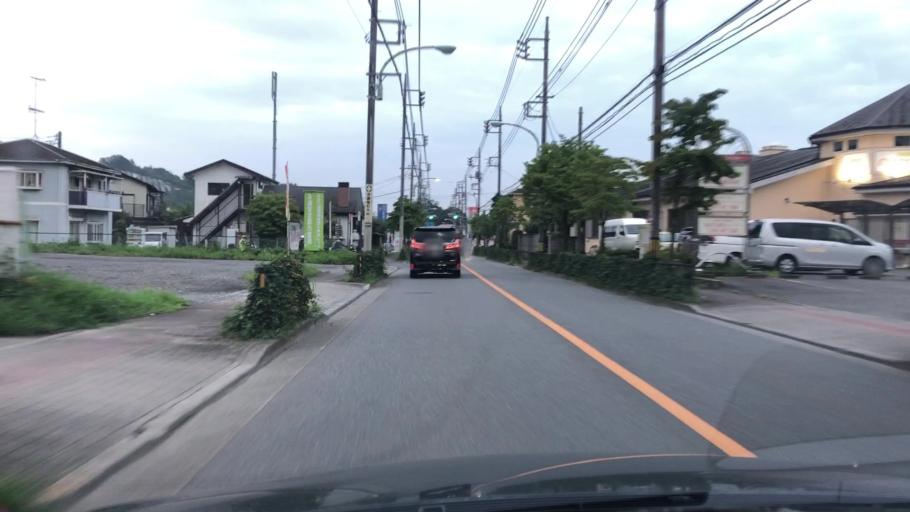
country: JP
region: Tokyo
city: Itsukaichi
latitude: 35.7430
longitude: 139.2515
